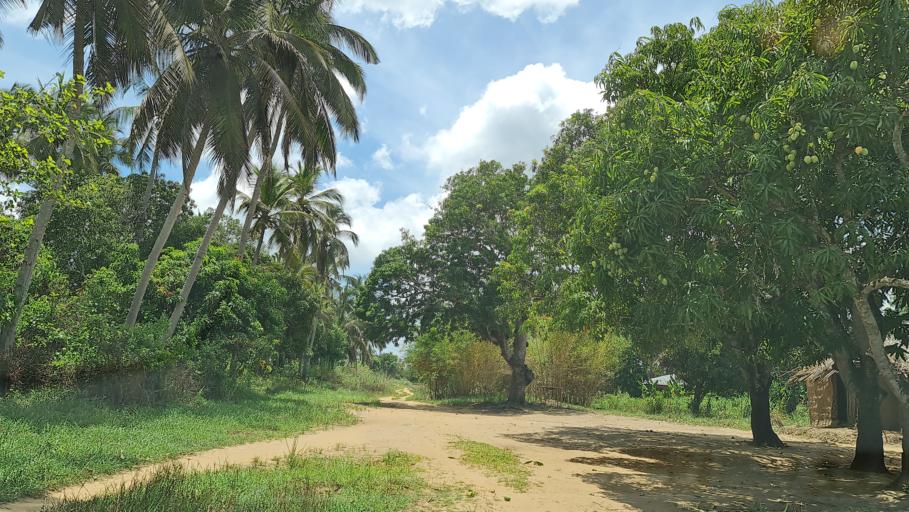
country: MZ
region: Zambezia
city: Quelimane
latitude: -17.5763
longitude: 37.3742
